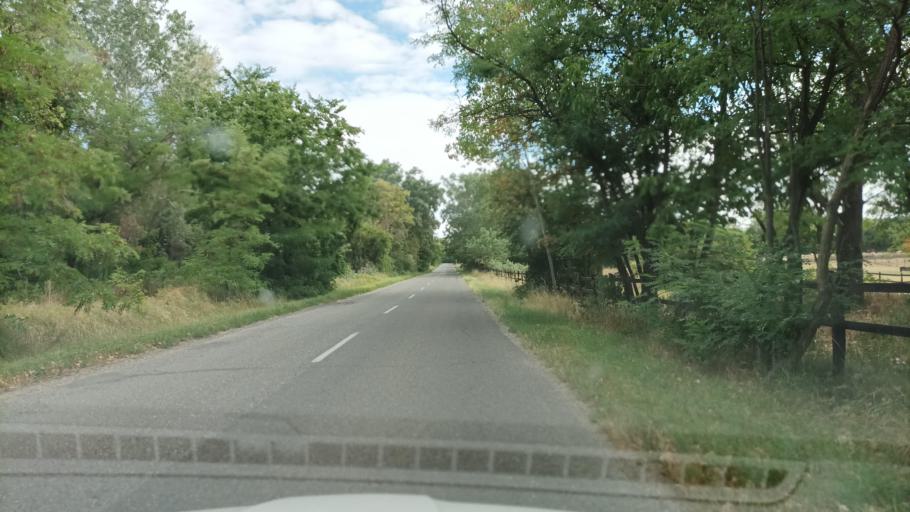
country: HU
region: Pest
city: Tahitotfalu
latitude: 47.7684
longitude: 19.1115
